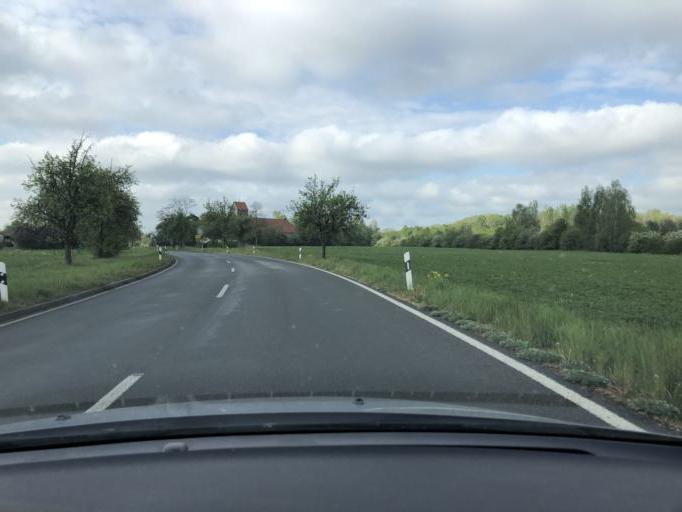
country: DE
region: Saxony
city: Deutzen
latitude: 51.1162
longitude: 12.4307
